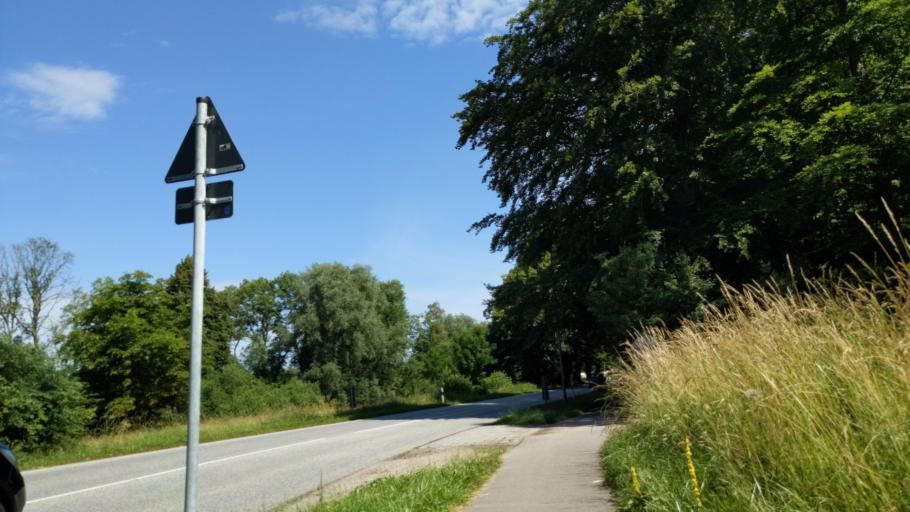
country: DE
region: Schleswig-Holstein
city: Ploen
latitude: 54.1508
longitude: 10.4017
